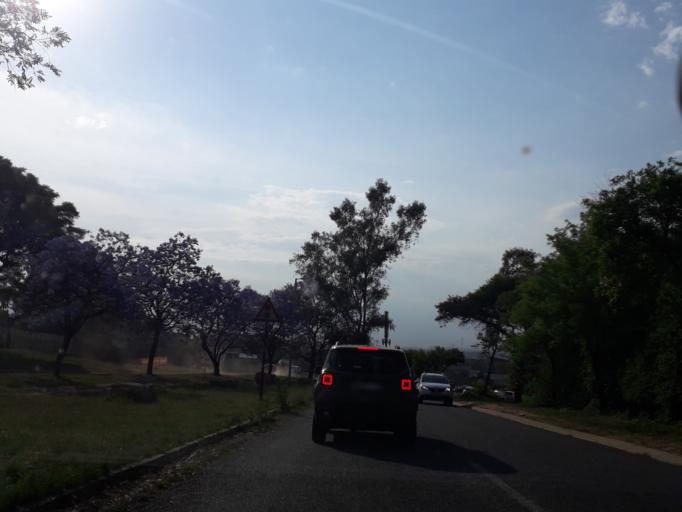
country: ZA
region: Gauteng
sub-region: City of Johannesburg Metropolitan Municipality
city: Roodepoort
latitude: -26.1127
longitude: 27.9454
